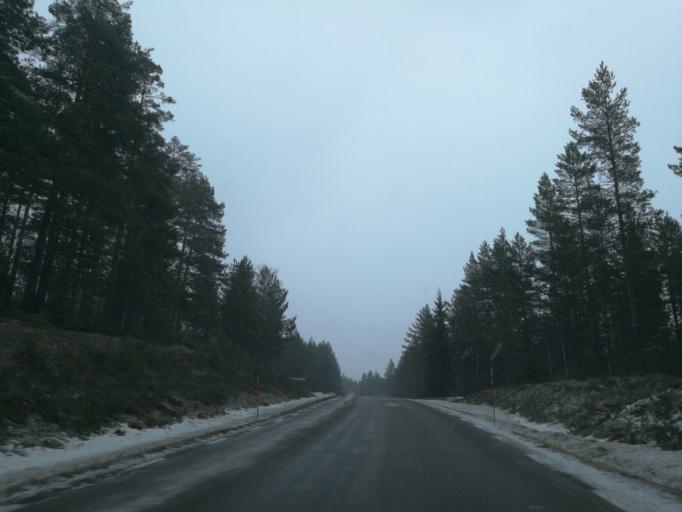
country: NO
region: Hedmark
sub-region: Grue
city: Kirkenaer
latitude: 60.6991
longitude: 12.5769
